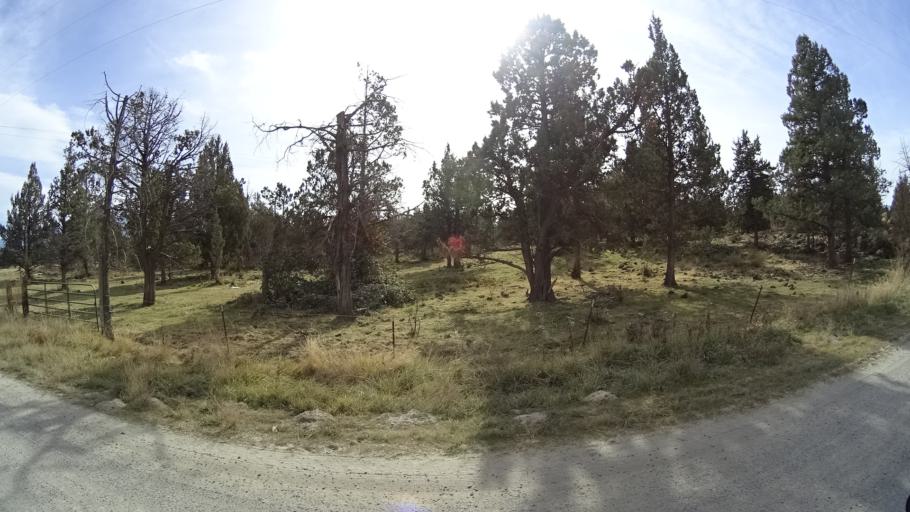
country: US
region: California
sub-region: Siskiyou County
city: Weed
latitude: 41.5954
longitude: -122.4123
